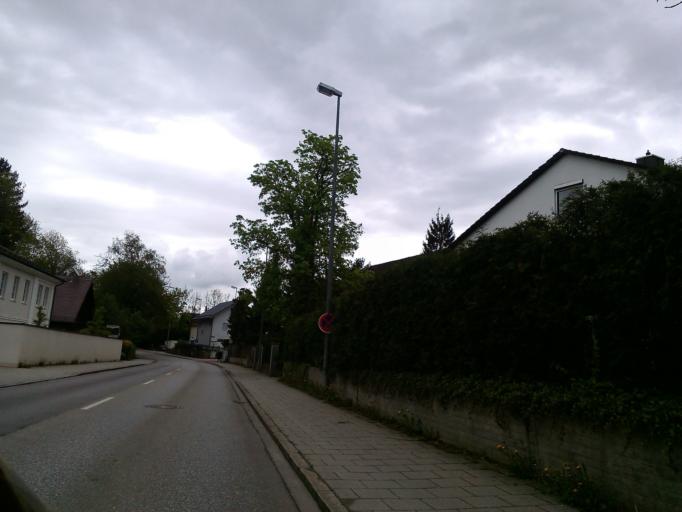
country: DE
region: Bavaria
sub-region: Upper Bavaria
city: Planegg
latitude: 48.0981
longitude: 11.4181
